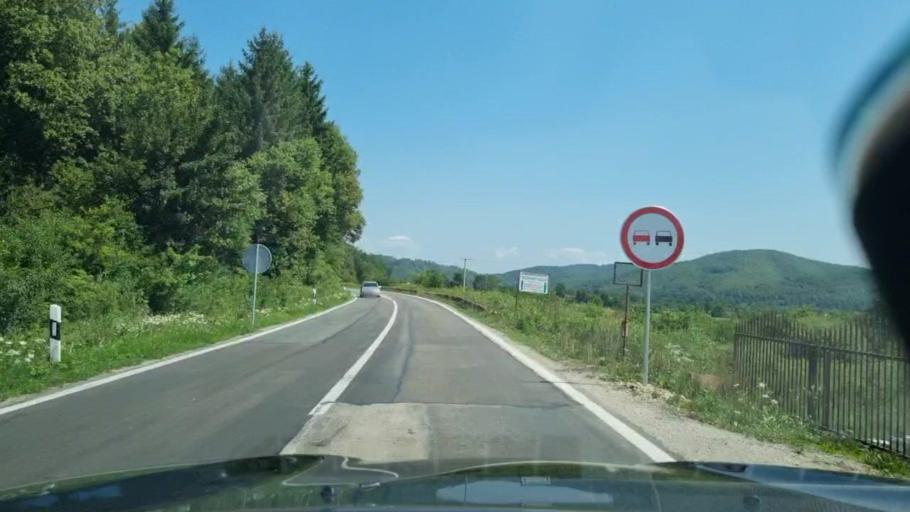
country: BA
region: Federation of Bosnia and Herzegovina
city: Sanski Most
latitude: 44.8083
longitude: 16.6476
